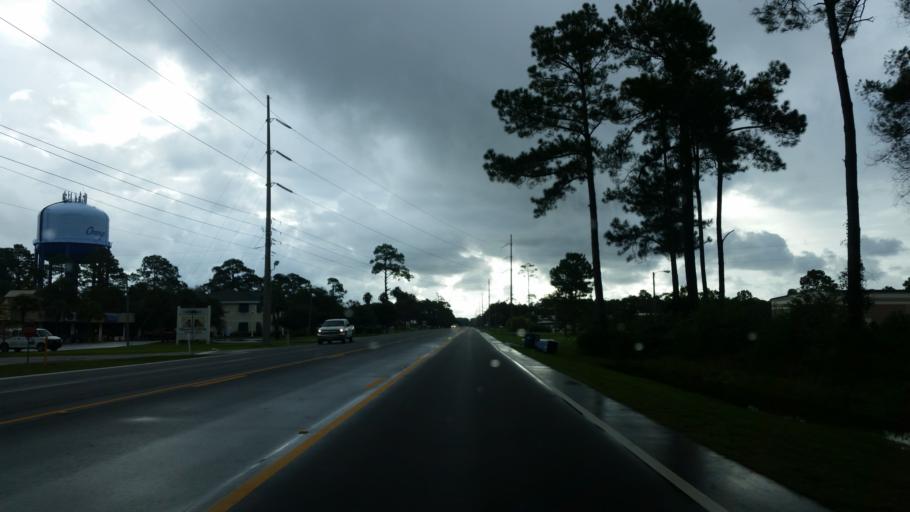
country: US
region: Alabama
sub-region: Baldwin County
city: Orange Beach
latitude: 30.2903
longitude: -87.5989
